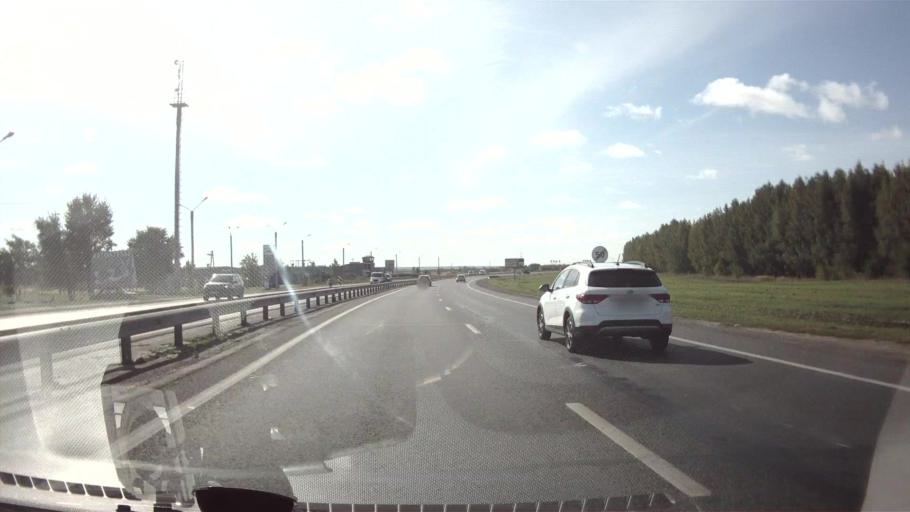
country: RU
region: Ulyanovsk
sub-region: Ulyanovskiy Rayon
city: Ulyanovsk
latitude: 54.2754
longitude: 48.2608
